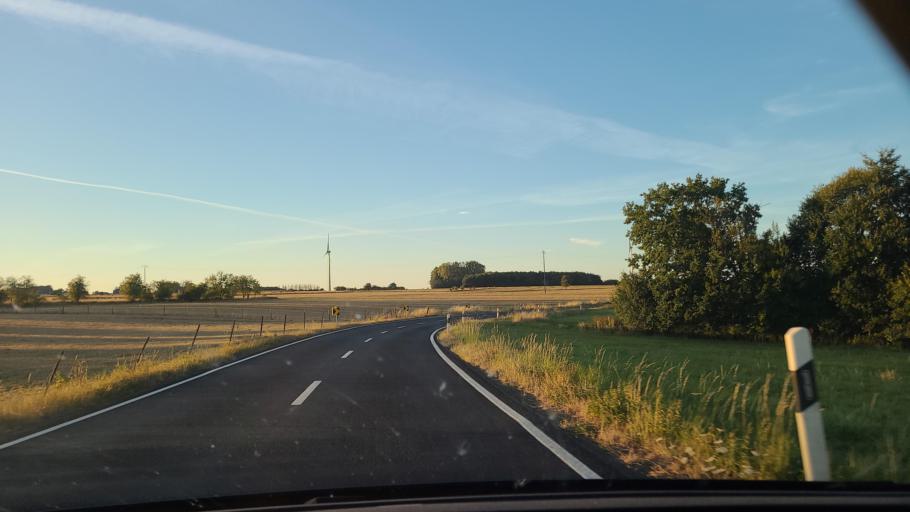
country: LU
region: Luxembourg
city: Hautcharage
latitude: 49.5946
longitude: 5.9134
